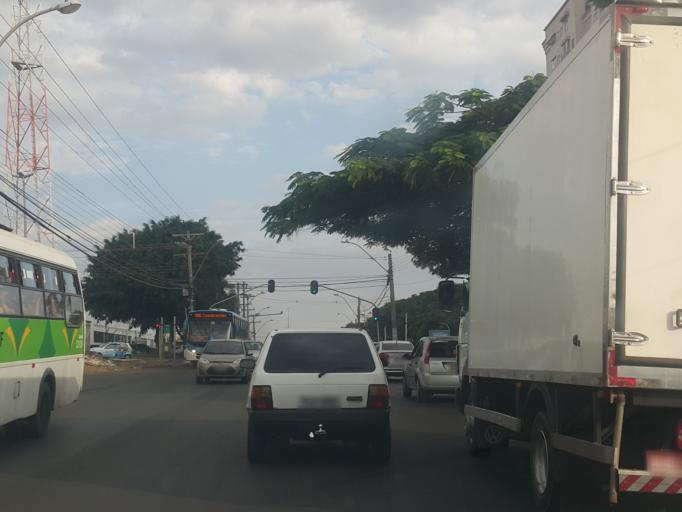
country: BR
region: Federal District
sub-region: Brasilia
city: Brasilia
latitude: -15.8318
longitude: -48.0613
